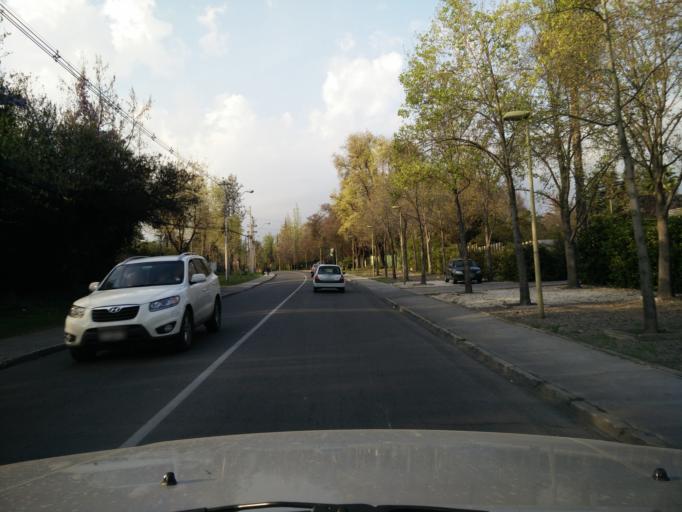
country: CL
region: Santiago Metropolitan
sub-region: Provincia de Santiago
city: Villa Presidente Frei, Nunoa, Santiago, Chile
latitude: -33.4001
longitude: -70.5323
